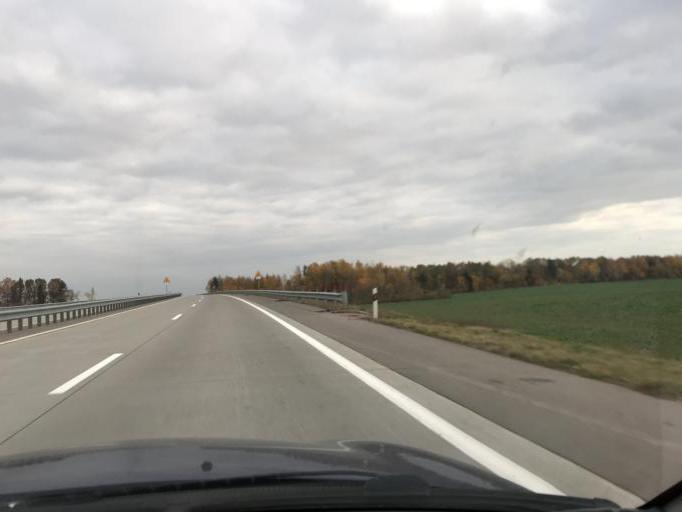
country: BY
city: Fanipol
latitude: 53.7689
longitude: 27.3649
